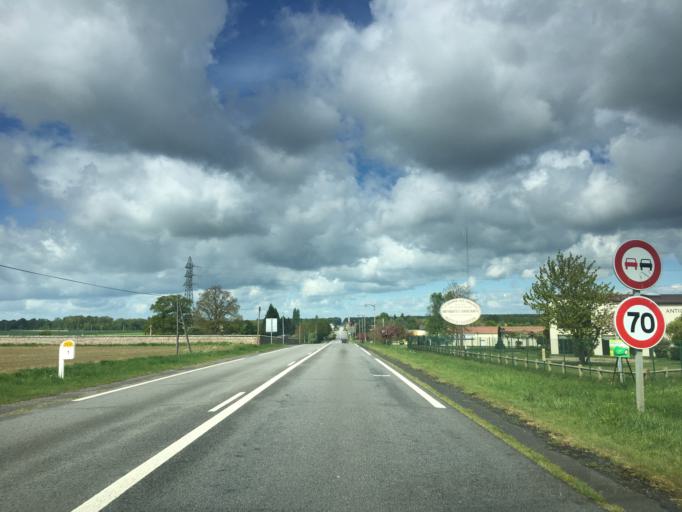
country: FR
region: Haute-Normandie
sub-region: Departement de l'Eure
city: Bourth
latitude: 48.7522
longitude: 0.7498
